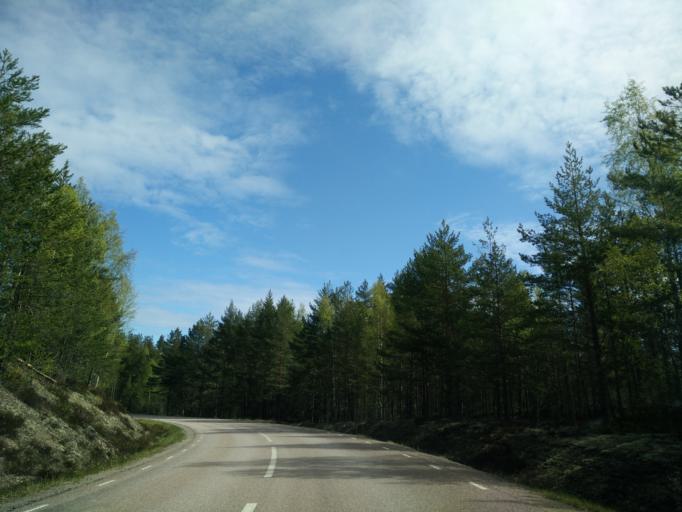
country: SE
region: Gaevleborg
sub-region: Hudiksvalls Kommun
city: Hudiksvall
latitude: 61.8347
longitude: 17.2640
